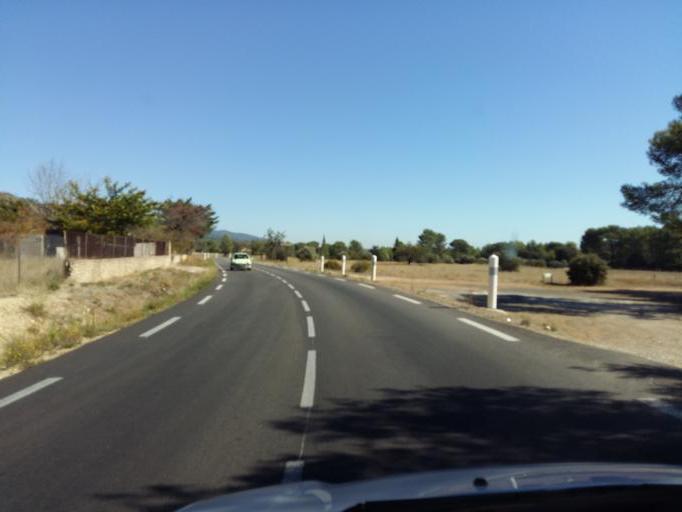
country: FR
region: Provence-Alpes-Cote d'Azur
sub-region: Departement du Vaucluse
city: Merindol
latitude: 43.7519
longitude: 5.2097
